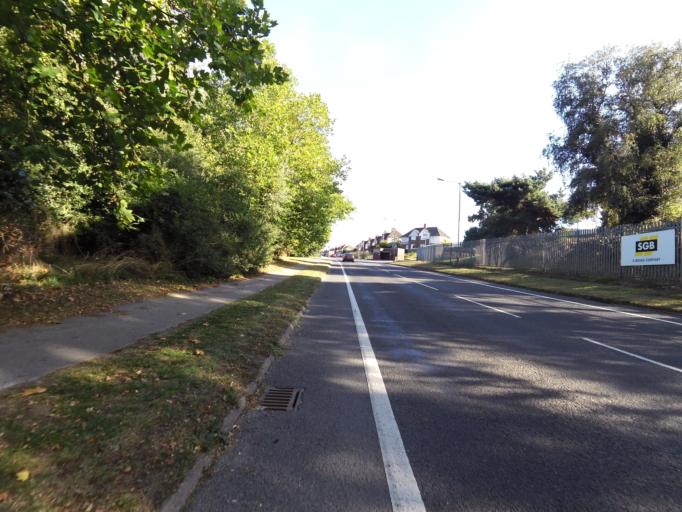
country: GB
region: England
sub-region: Suffolk
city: Ipswich
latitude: 52.0387
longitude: 1.1703
